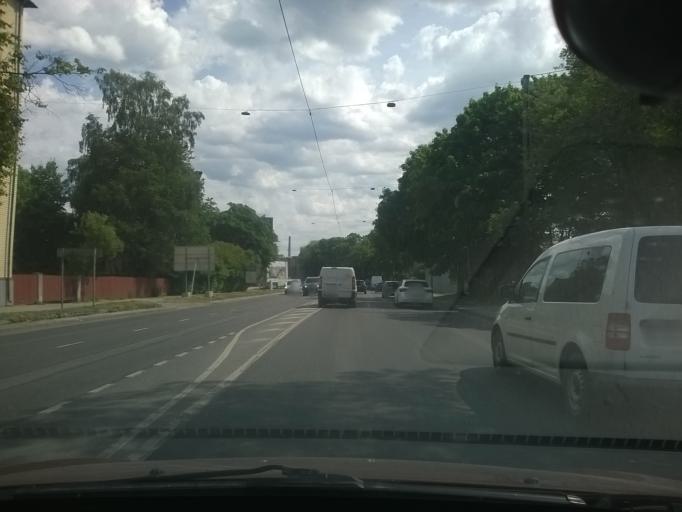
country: EE
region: Harju
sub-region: Tallinna linn
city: Tallinn
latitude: 59.4283
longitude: 24.7097
